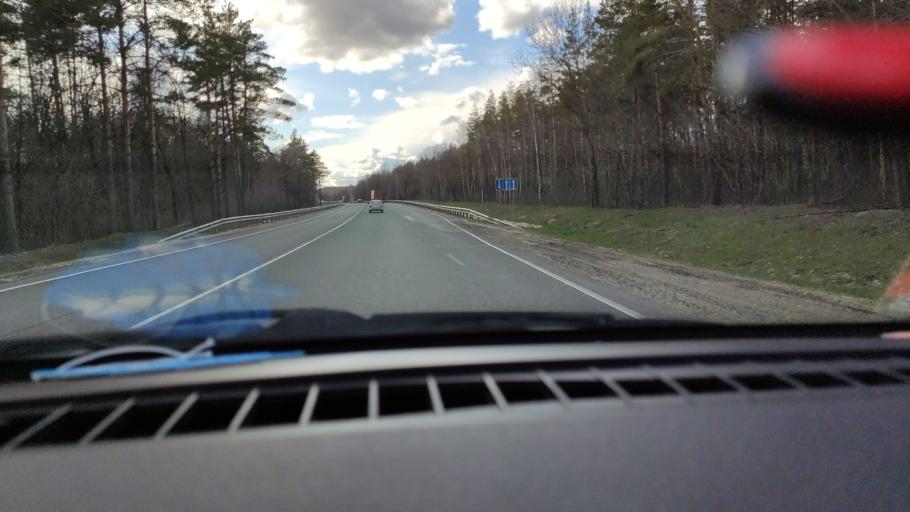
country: RU
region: Saratov
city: Vol'sk
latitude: 52.1065
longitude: 47.4252
